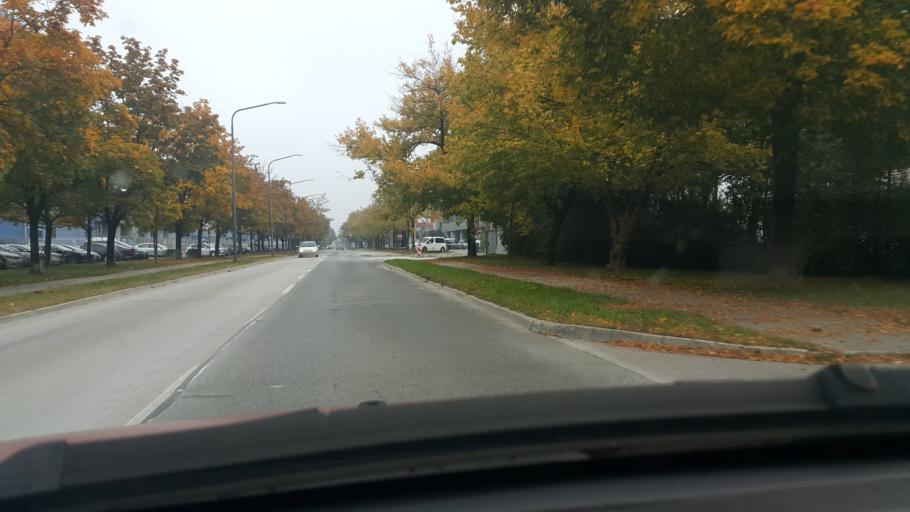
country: SI
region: Ljubljana
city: Ljubljana
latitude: 46.0772
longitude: 14.5005
